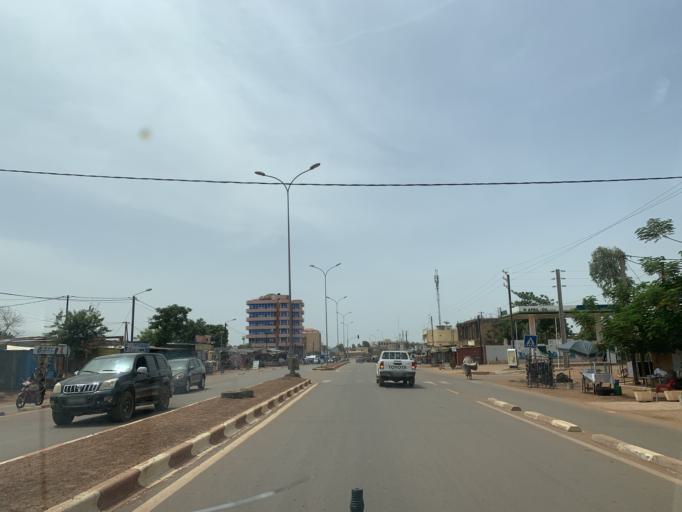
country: BF
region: Centre
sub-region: Kadiogo Province
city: Ouagadougou
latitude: 12.3389
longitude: -1.5107
